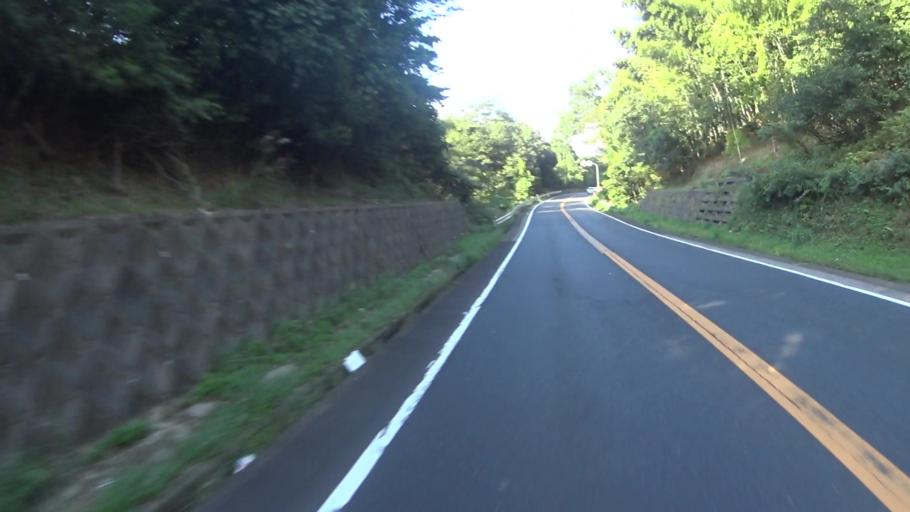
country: JP
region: Hyogo
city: Toyooka
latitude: 35.5915
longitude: 134.8739
